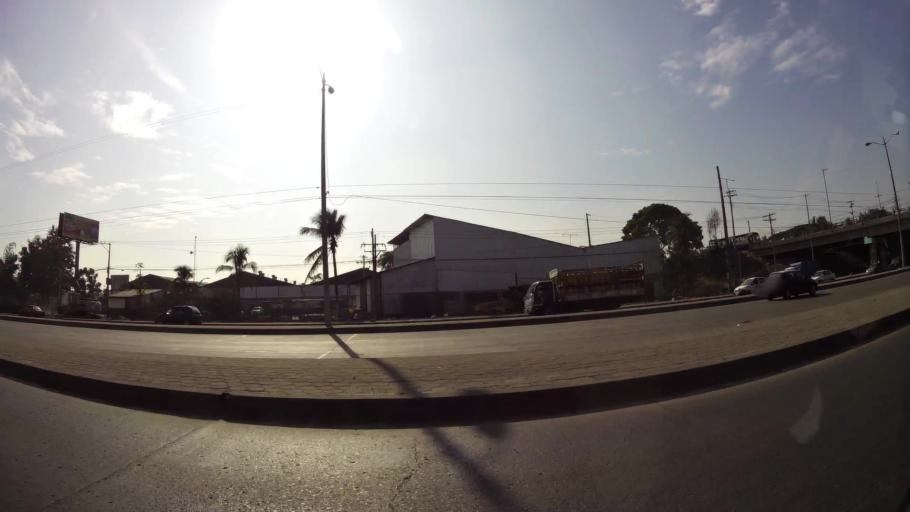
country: EC
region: Guayas
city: Santa Lucia
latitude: -2.0815
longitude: -79.9394
